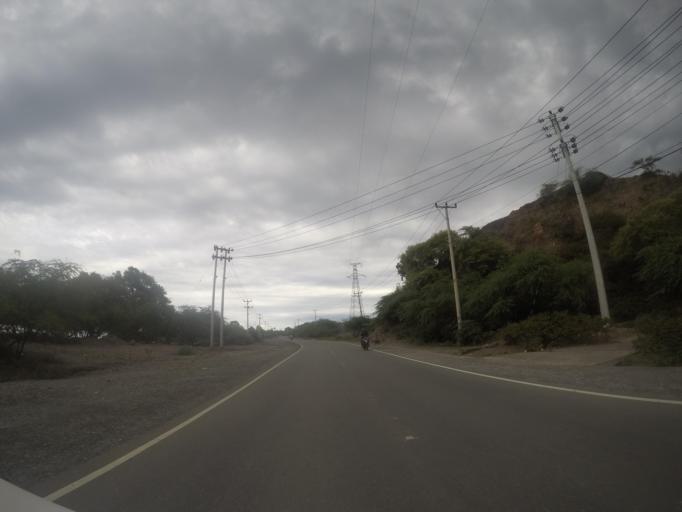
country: TL
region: Liquica
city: Liquica
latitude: -8.5730
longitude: 125.3775
